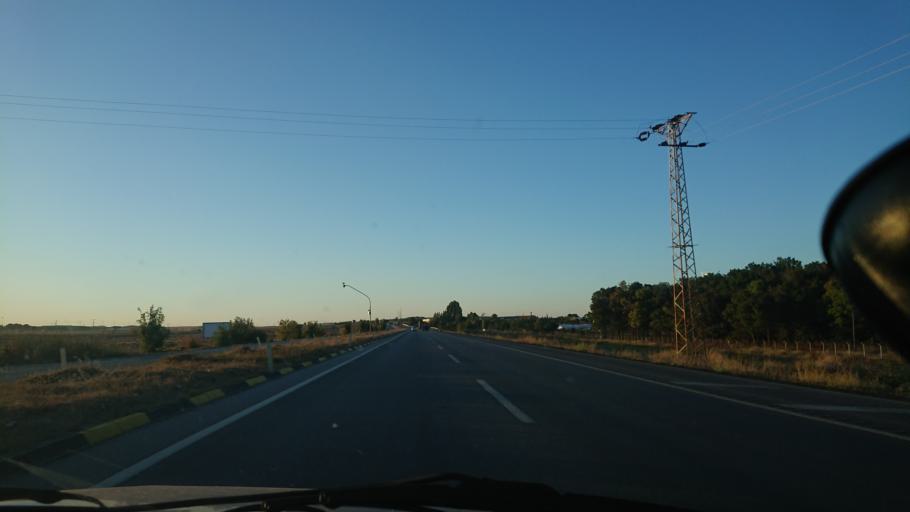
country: TR
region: Eskisehir
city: Mahmudiye
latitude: 39.4775
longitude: 30.9906
